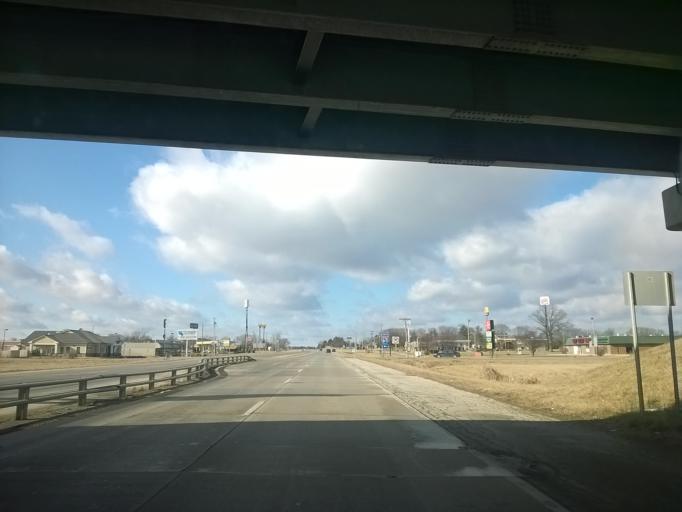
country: US
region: Indiana
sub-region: Johnson County
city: Franklin
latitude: 39.4833
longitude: -86.0140
